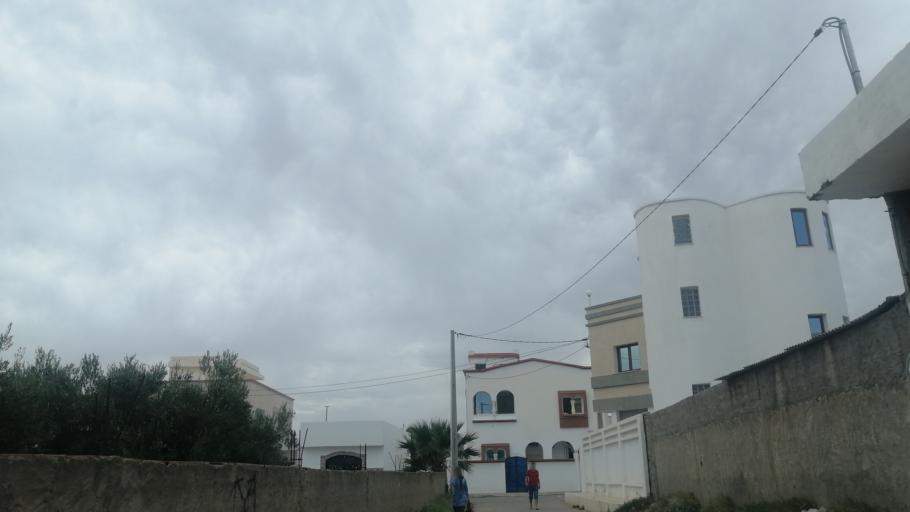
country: TN
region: Al Qayrawan
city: Sbikha
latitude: 36.1254
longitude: 10.0921
